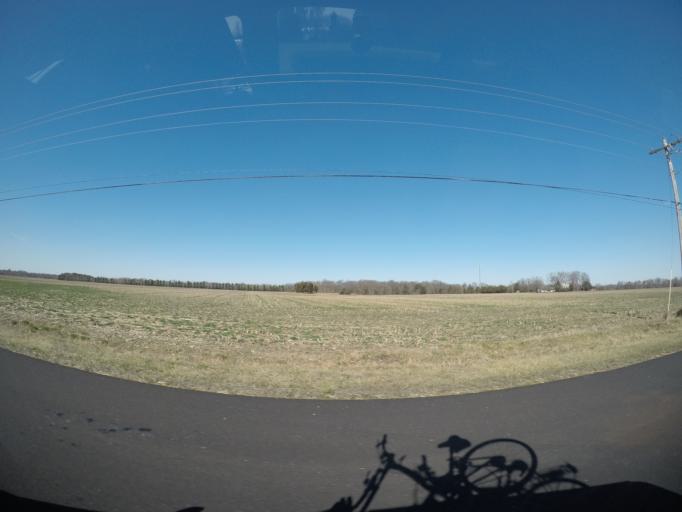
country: US
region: Delaware
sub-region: New Castle County
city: Townsend
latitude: 39.3594
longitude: -75.8299
